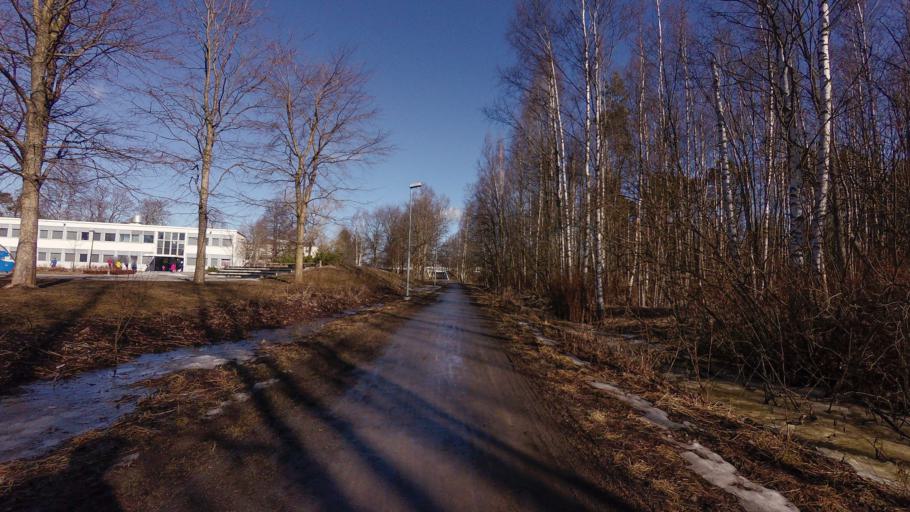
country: FI
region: Uusimaa
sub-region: Helsinki
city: Vantaa
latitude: 60.1768
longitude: 25.0561
